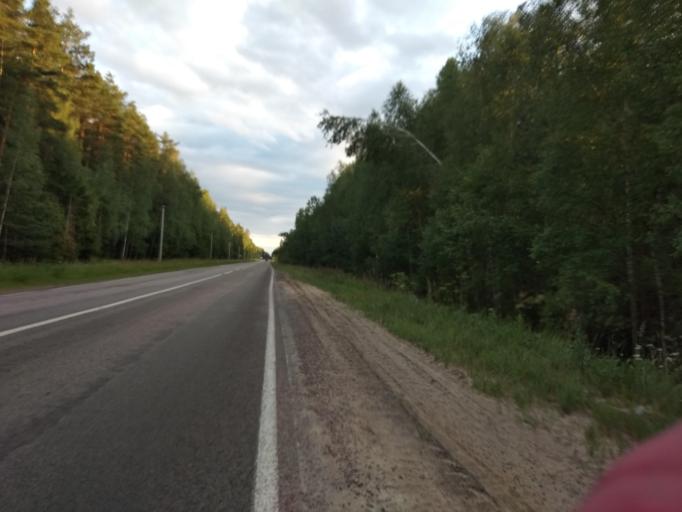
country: RU
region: Moskovskaya
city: Misheronskiy
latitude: 55.6241
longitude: 39.7330
